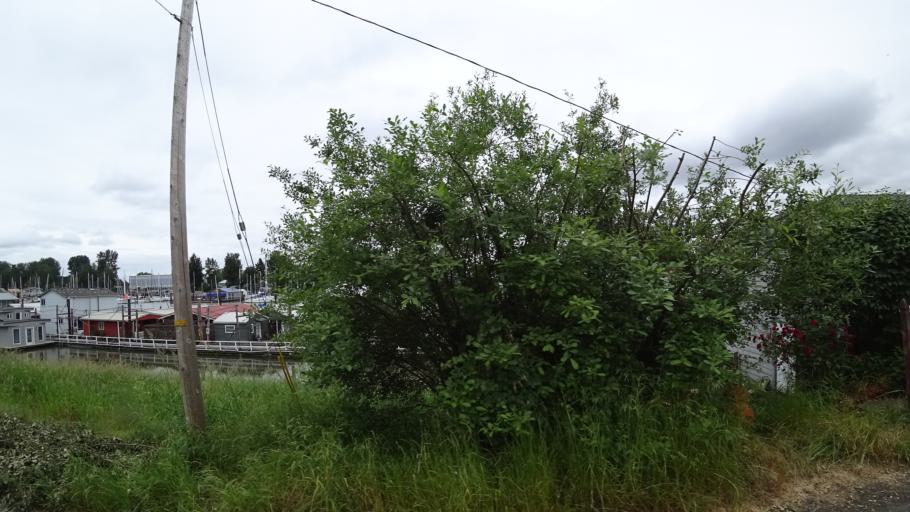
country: US
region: Washington
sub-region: Clark County
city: Vancouver
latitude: 45.6020
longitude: -122.6622
